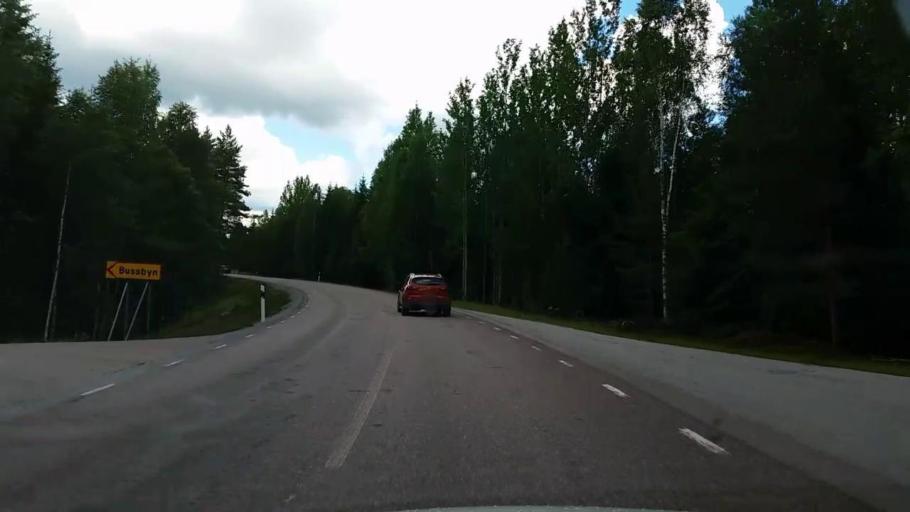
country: SE
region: Vaestmanland
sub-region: Fagersta Kommun
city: Fagersta
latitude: 59.8821
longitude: 15.8368
